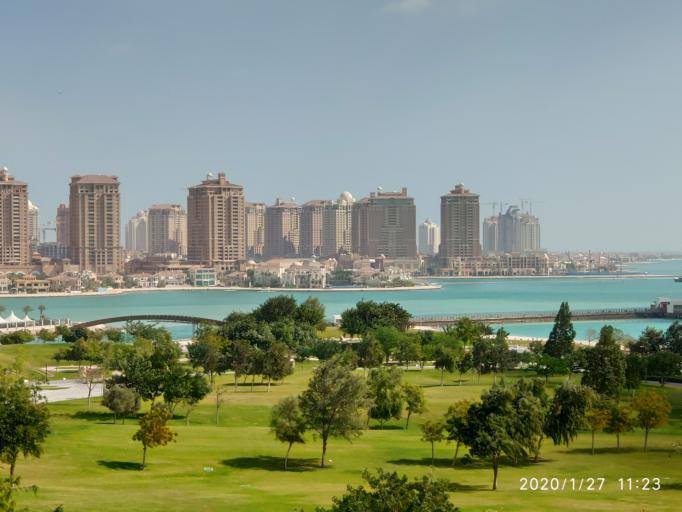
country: QA
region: Baladiyat ad Dawhah
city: Doha
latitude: 25.3634
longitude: 51.5253
